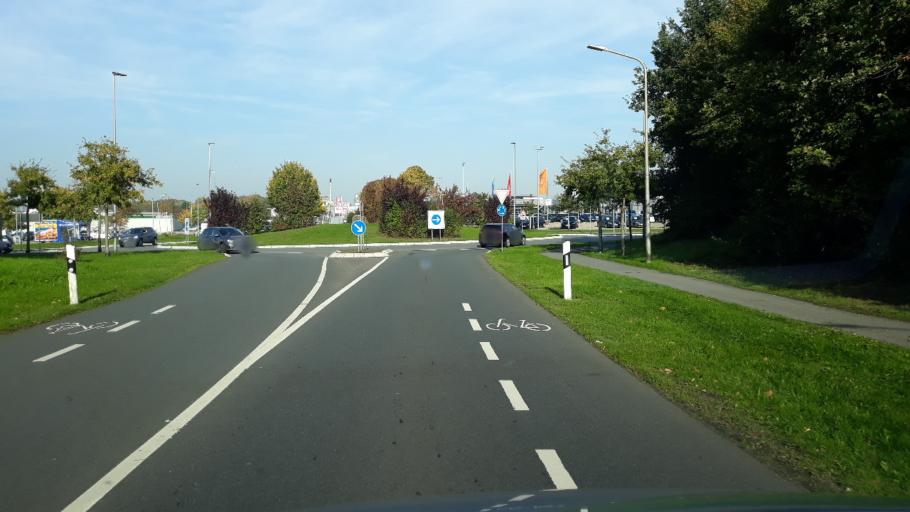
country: DE
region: Schleswig-Holstein
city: Schleswig
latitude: 54.5301
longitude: 9.5731
